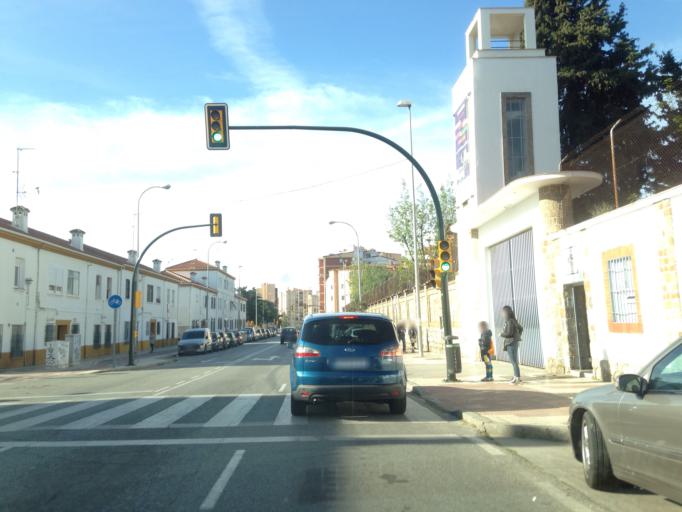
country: ES
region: Andalusia
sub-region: Provincia de Malaga
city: Malaga
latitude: 36.7253
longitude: -4.4391
